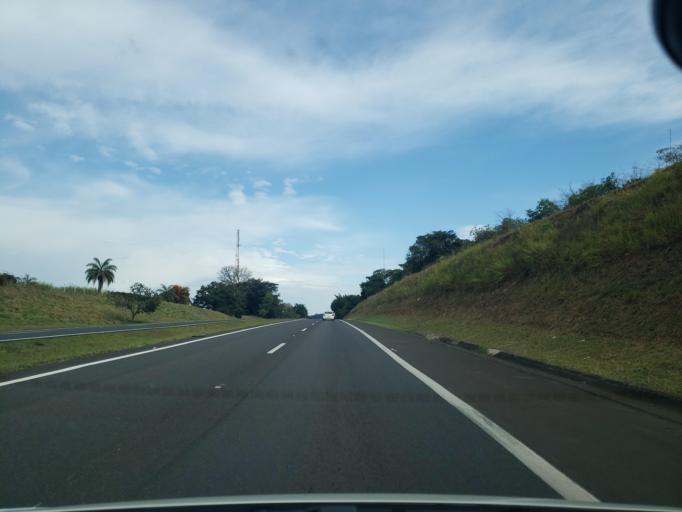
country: BR
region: Sao Paulo
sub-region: Itirapina
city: Itirapina
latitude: -22.2756
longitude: -47.9717
